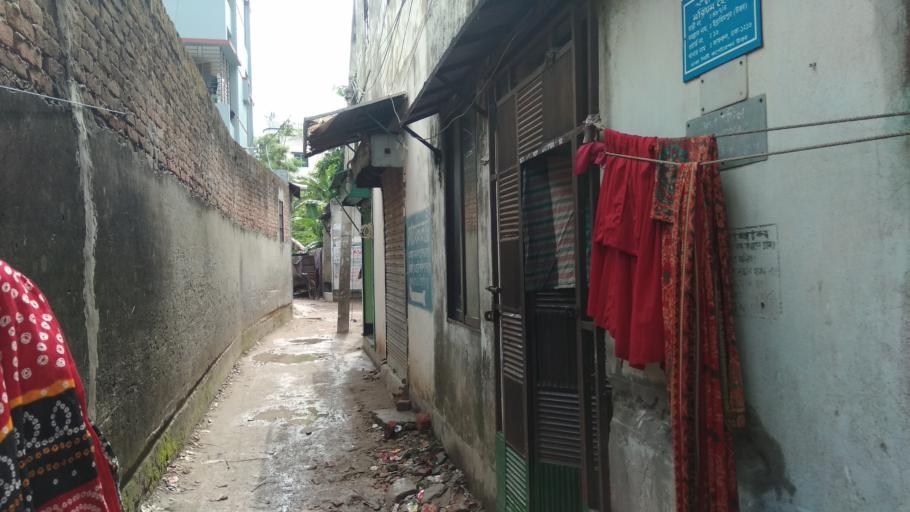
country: BD
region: Dhaka
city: Azimpur
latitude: 23.7994
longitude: 90.3791
